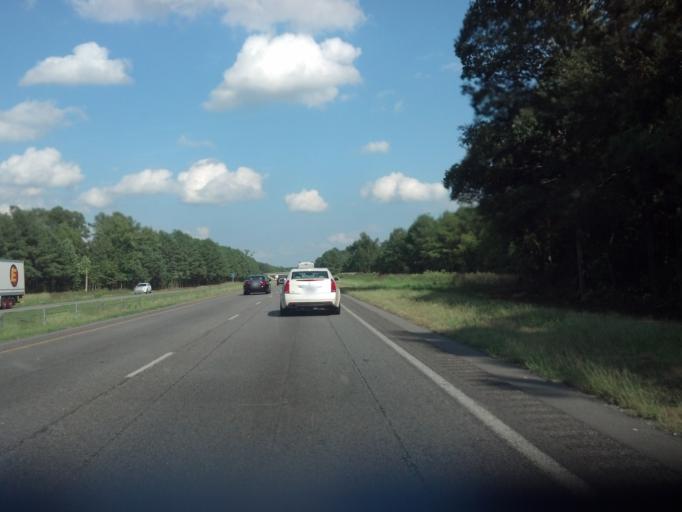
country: US
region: North Carolina
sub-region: Nash County
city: Rocky Mount
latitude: 35.9359
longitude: -77.7394
